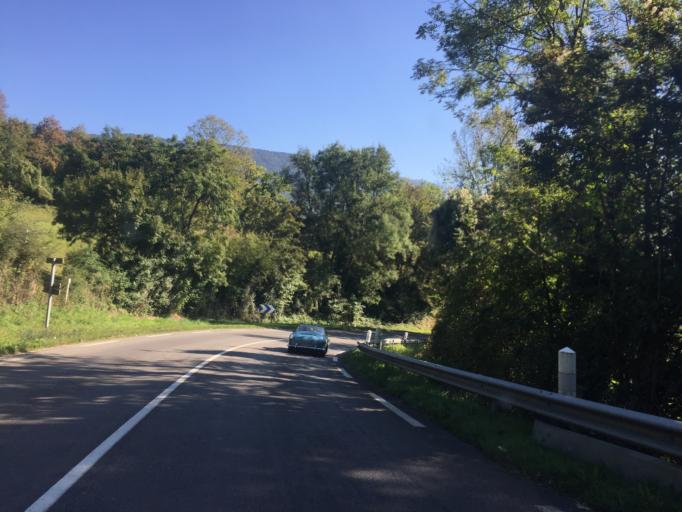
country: FR
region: Rhone-Alpes
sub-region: Departement de la Haute-Savoie
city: Viuz-la-Chiesaz
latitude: 45.8392
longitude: 6.0593
